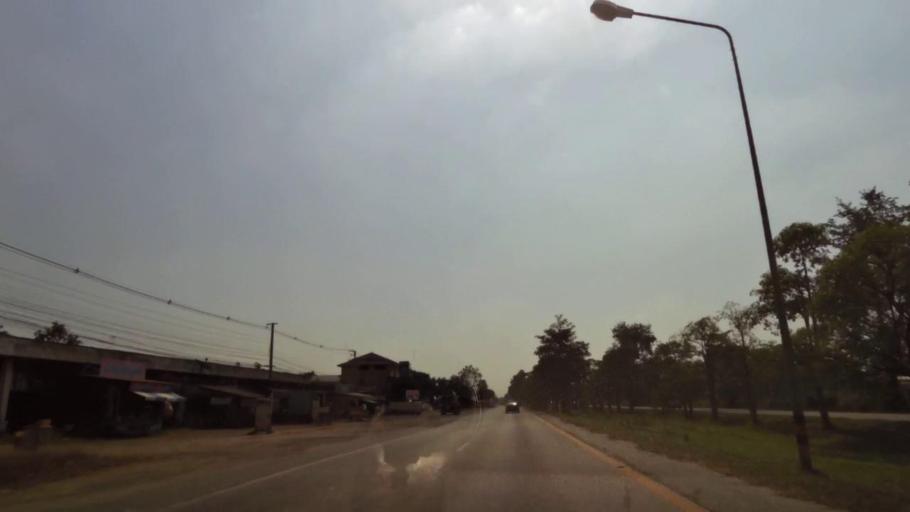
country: TH
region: Phichit
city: Wachira Barami
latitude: 16.5040
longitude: 100.1436
